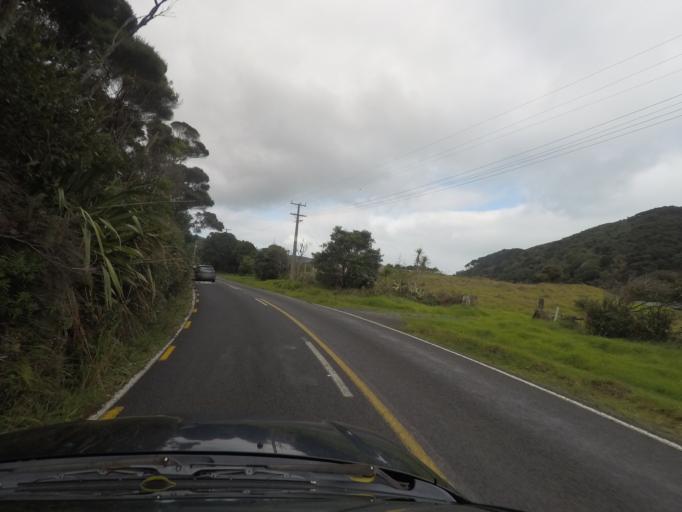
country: NZ
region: Auckland
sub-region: Auckland
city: Muriwai Beach
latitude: -36.8823
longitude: 174.4510
